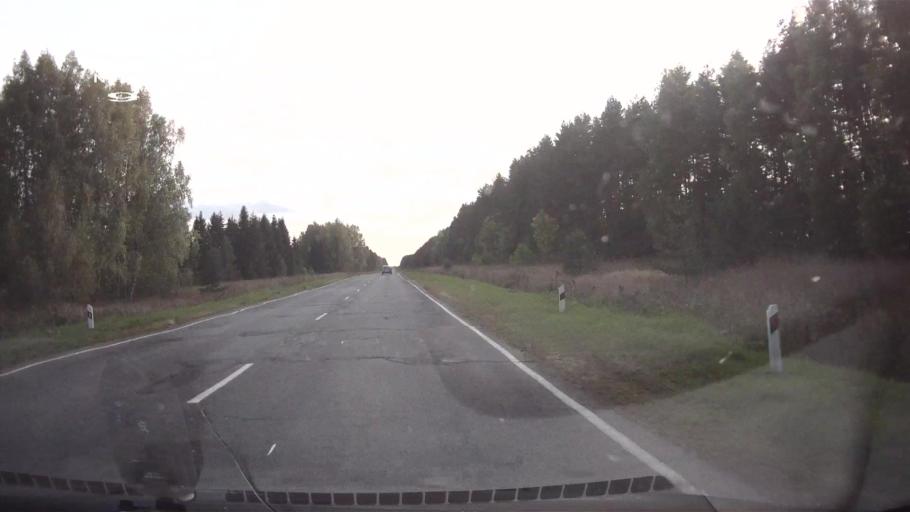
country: RU
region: Mariy-El
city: Kuzhener
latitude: 56.8337
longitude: 48.7308
